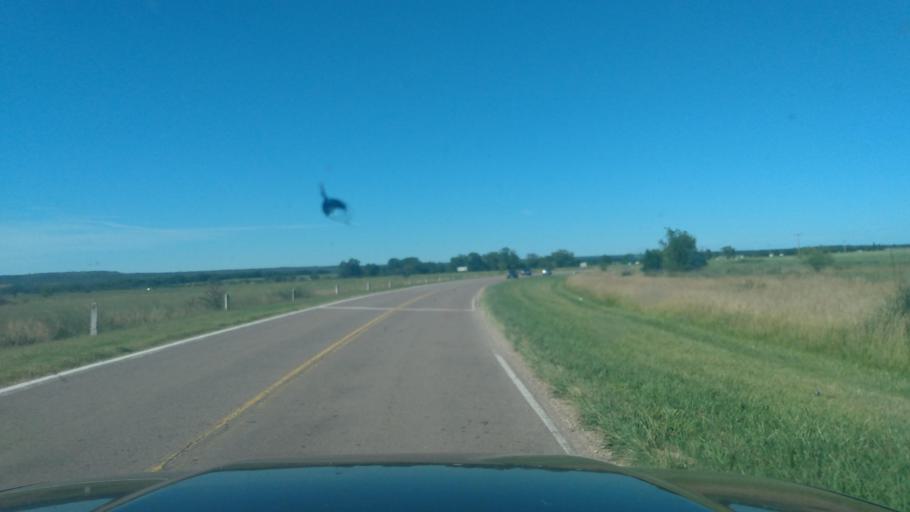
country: AR
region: La Pampa
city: Doblas
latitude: -37.3110
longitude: -64.2891
